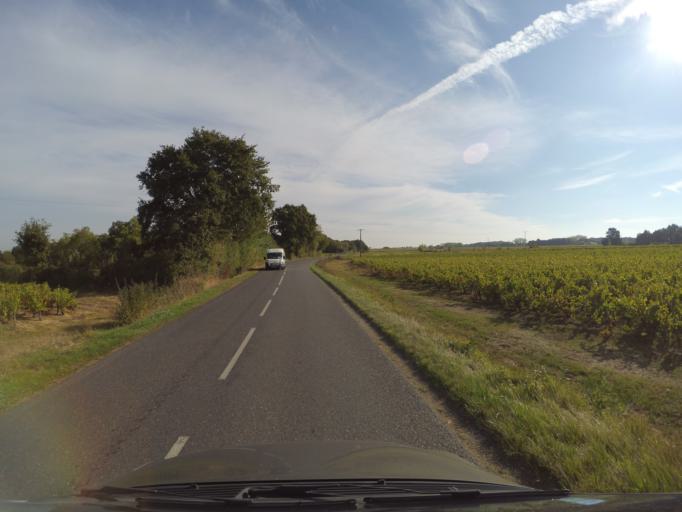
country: FR
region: Pays de la Loire
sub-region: Departement de la Loire-Atlantique
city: Mouzillon
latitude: 47.1267
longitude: -1.2696
